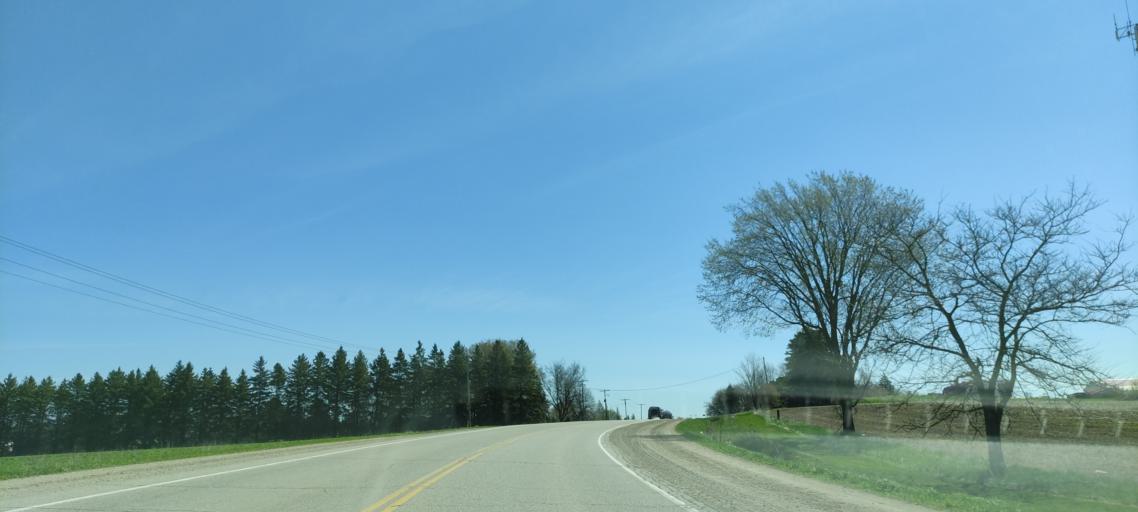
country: CA
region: Ontario
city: Waterloo
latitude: 43.6037
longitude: -80.6009
